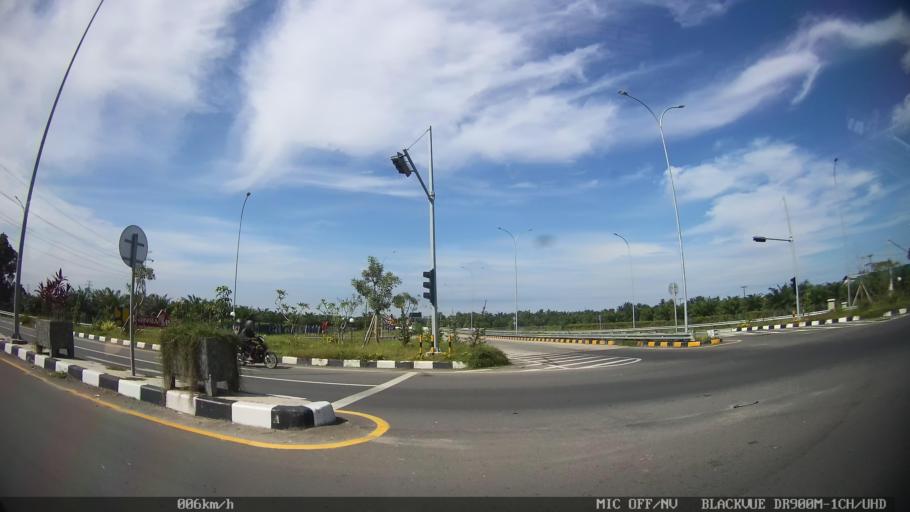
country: ID
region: North Sumatra
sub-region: Kabupaten Langkat
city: Stabat
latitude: 3.7330
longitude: 98.4911
